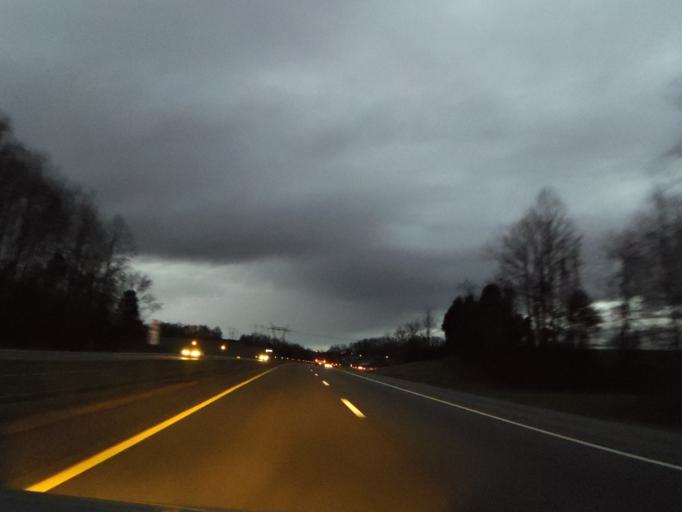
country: US
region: Tennessee
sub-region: Washington County
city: Gray
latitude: 36.4246
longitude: -82.5109
